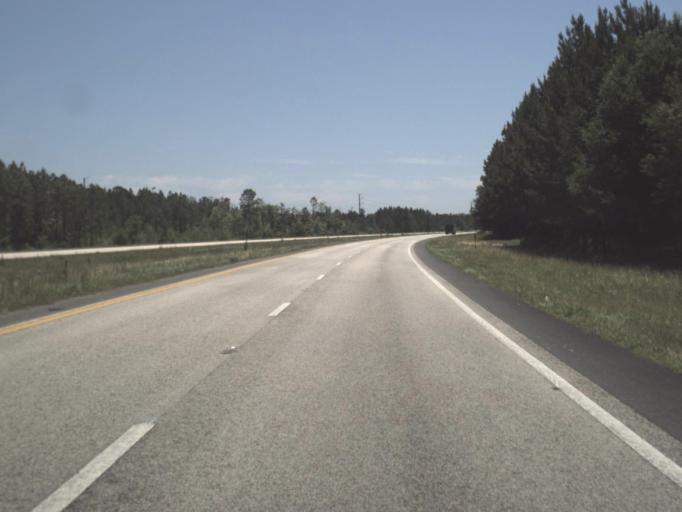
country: US
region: Florida
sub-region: Clay County
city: Bellair-Meadowbrook Terrace
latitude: 30.2206
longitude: -81.8391
